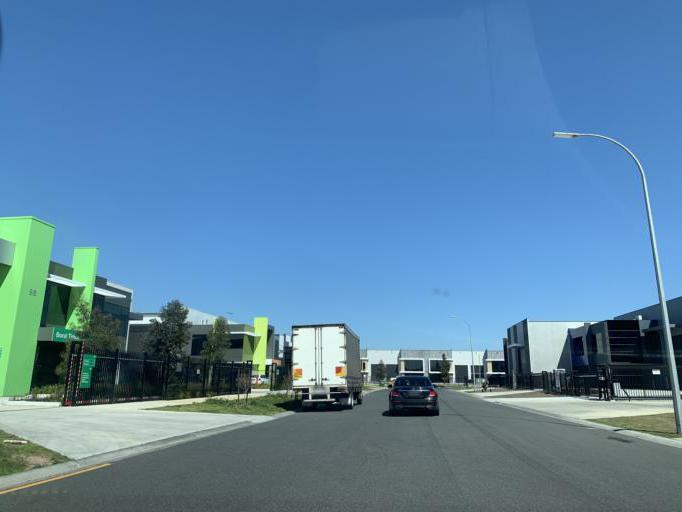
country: AU
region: Victoria
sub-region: Greater Dandenong
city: Keysborough
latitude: -38.0078
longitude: 145.1873
